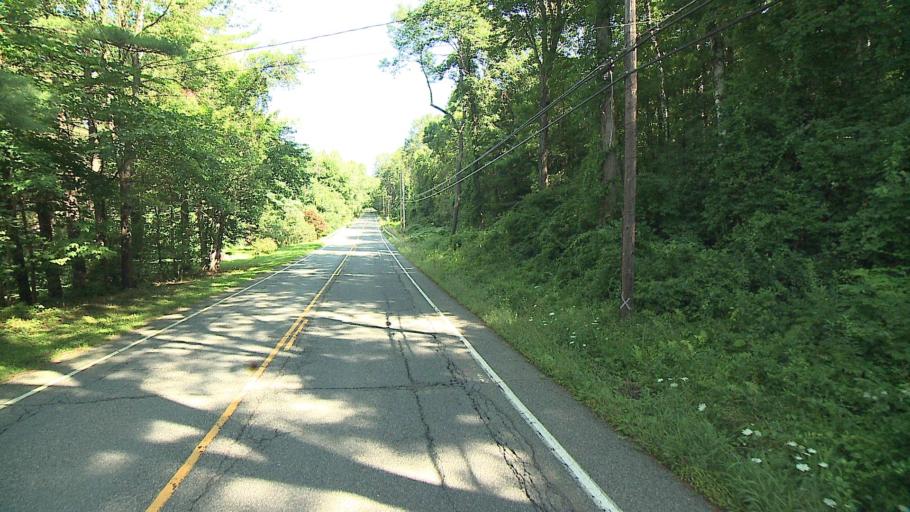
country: US
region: Connecticut
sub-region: Litchfield County
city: Canaan
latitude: 42.0157
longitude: -73.4295
